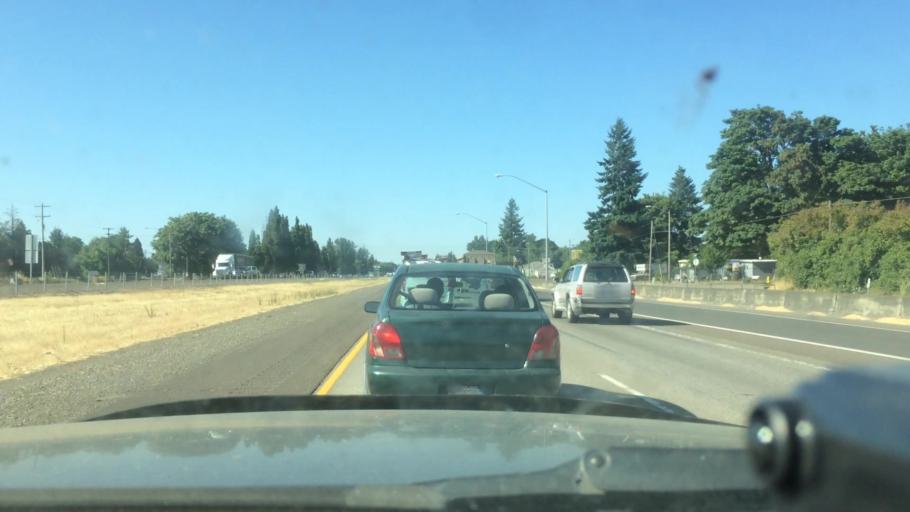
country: US
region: Oregon
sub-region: Linn County
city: Millersburg
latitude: 44.6503
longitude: -123.0616
